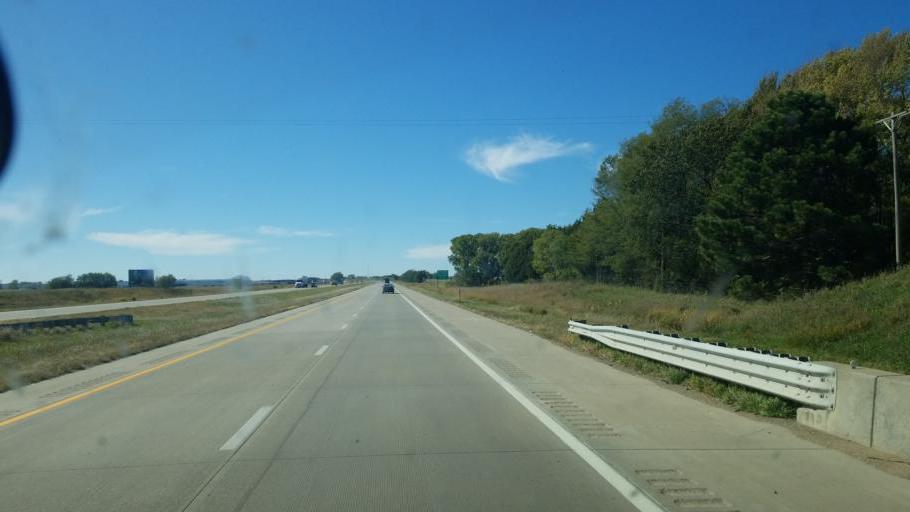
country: US
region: Kansas
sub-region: Dickinson County
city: Abilene
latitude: 38.9376
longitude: -97.2417
